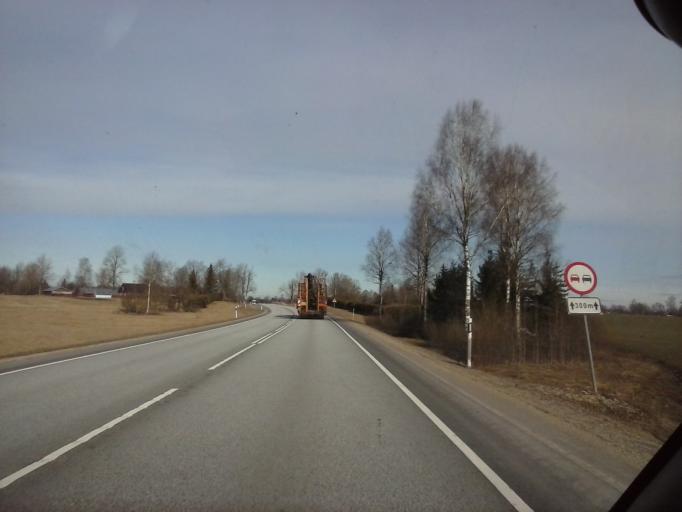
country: EE
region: Jaervamaa
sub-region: Paide linn
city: Paide
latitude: 58.8612
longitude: 25.7156
